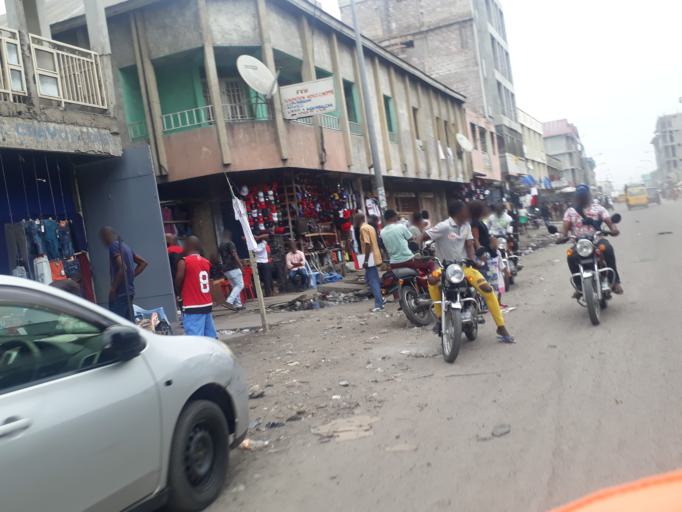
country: CD
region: Kinshasa
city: Kinshasa
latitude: -4.3134
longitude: 15.3095
